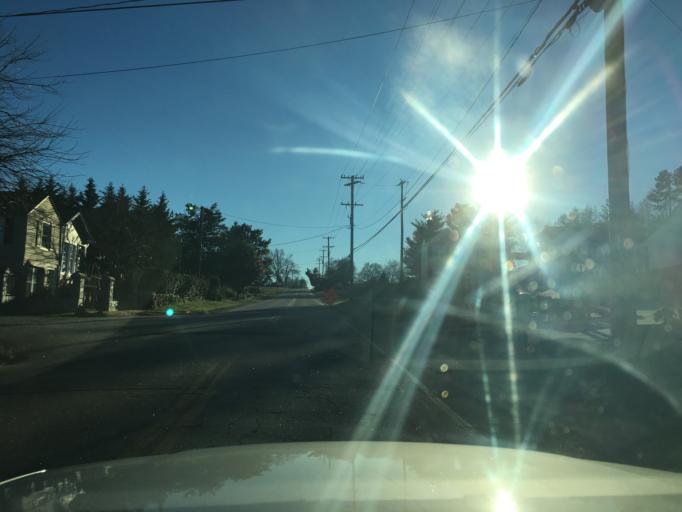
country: US
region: South Carolina
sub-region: Greenville County
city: Greer
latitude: 34.9351
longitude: -82.2443
